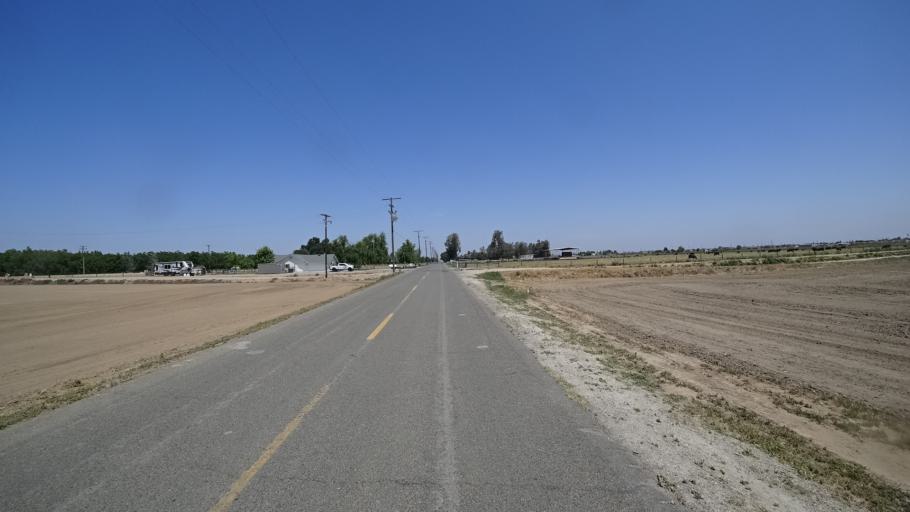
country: US
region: California
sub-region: Kings County
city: Armona
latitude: 36.3051
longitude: -119.6911
